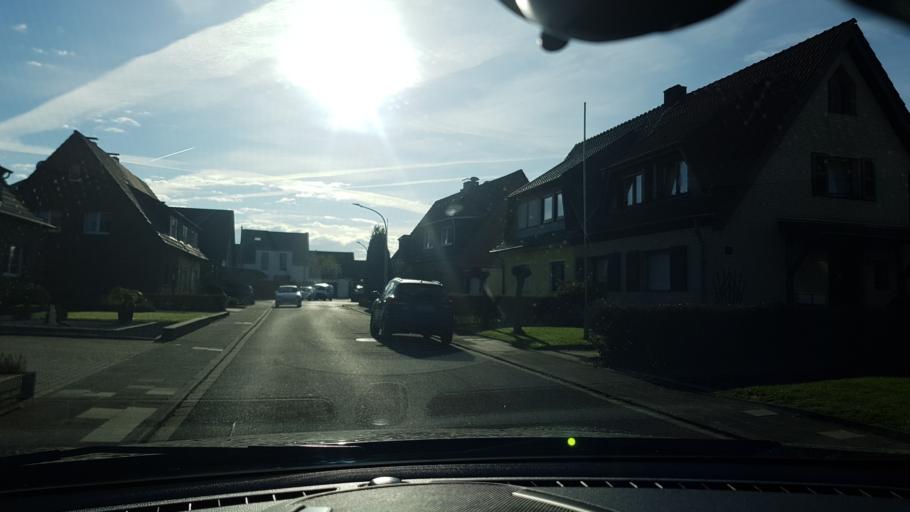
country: DE
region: North Rhine-Westphalia
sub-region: Regierungsbezirk Dusseldorf
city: Grevenbroich
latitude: 51.1170
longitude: 6.5604
